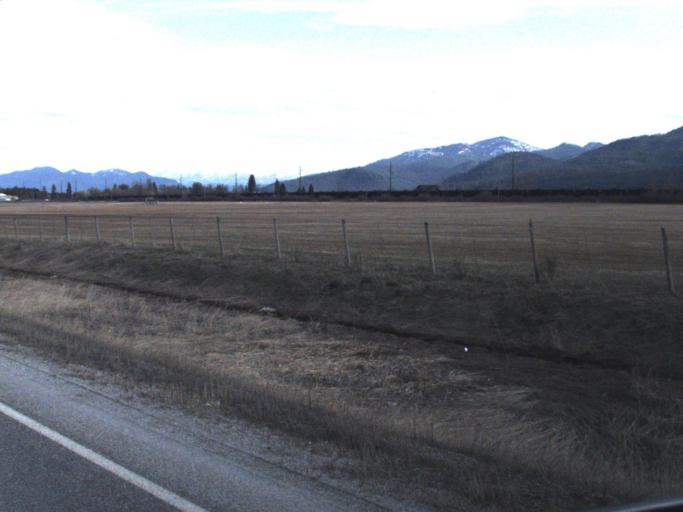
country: US
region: Washington
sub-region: Pend Oreille County
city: Newport
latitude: 48.3230
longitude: -117.2958
